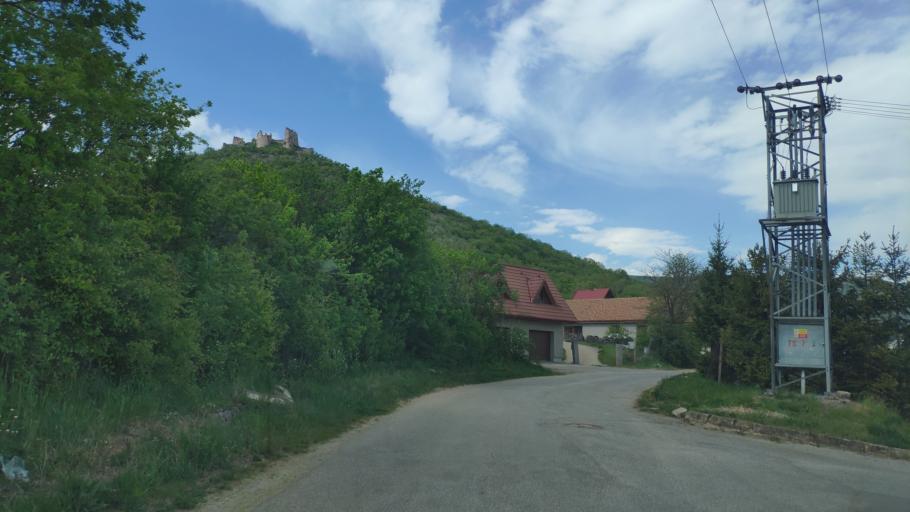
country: SK
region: Kosicky
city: Medzev
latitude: 48.6056
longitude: 20.8769
